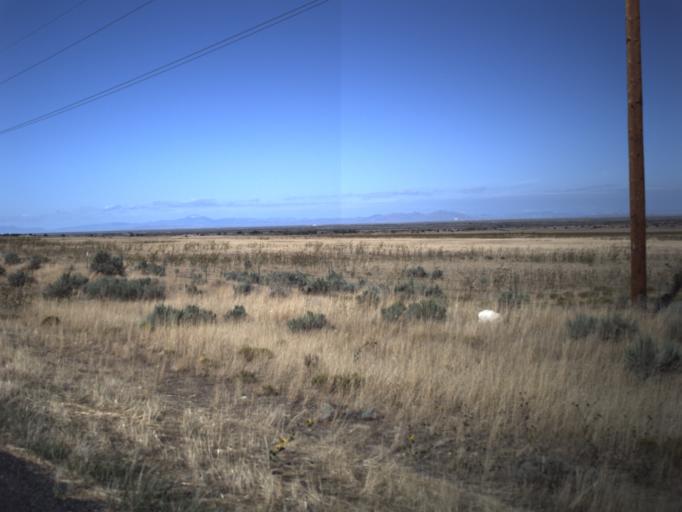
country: US
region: Utah
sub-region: Millard County
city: Delta
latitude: 39.4636
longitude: -112.2848
